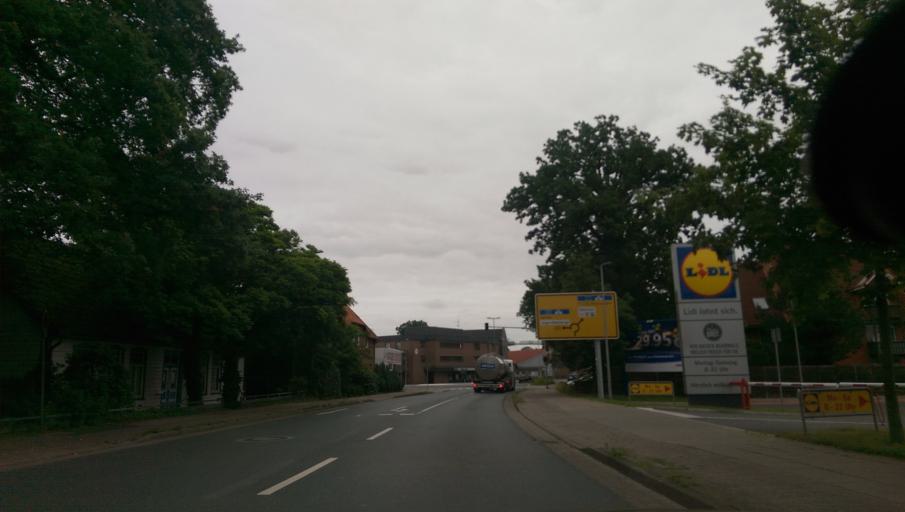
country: DE
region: Lower Saxony
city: Rotenburg
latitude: 53.1025
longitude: 9.3978
